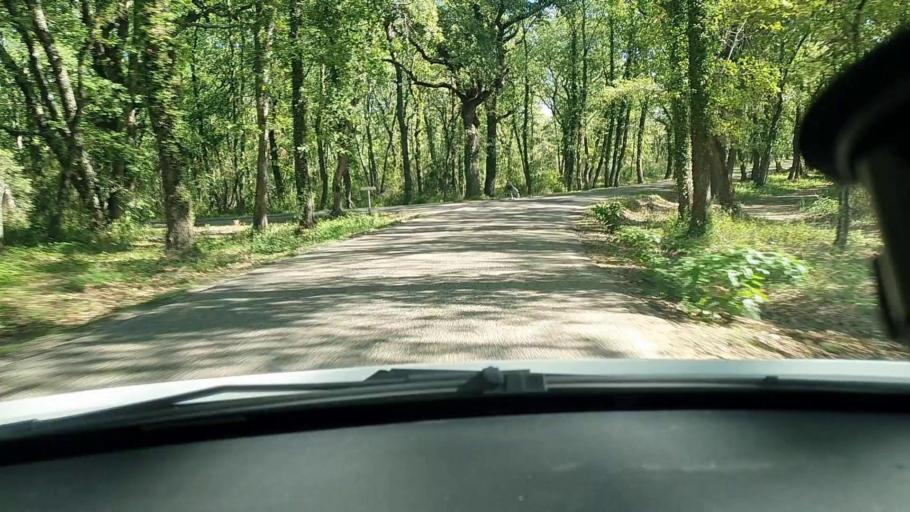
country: FR
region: Languedoc-Roussillon
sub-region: Departement du Gard
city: Saint-Julien-de-Peyrolas
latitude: 44.2781
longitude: 4.5395
